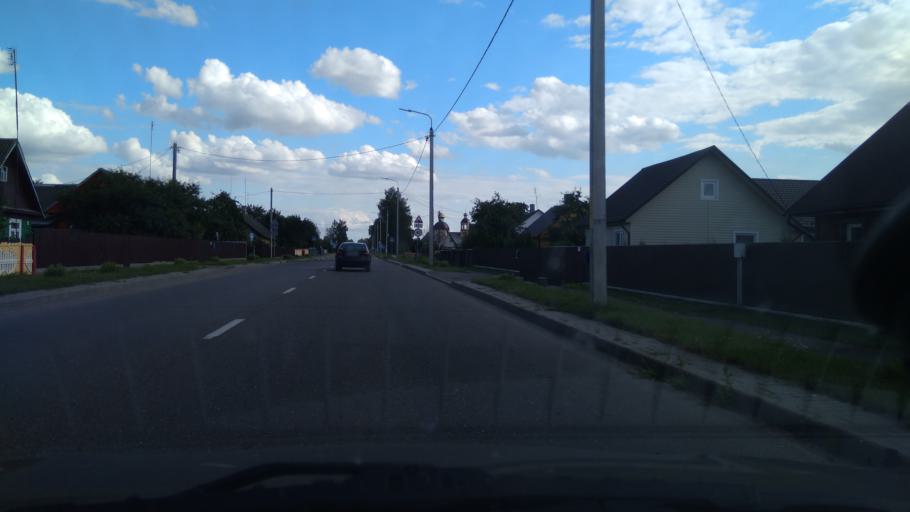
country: BY
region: Grodnenskaya
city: Masty
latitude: 53.3941
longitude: 24.5364
